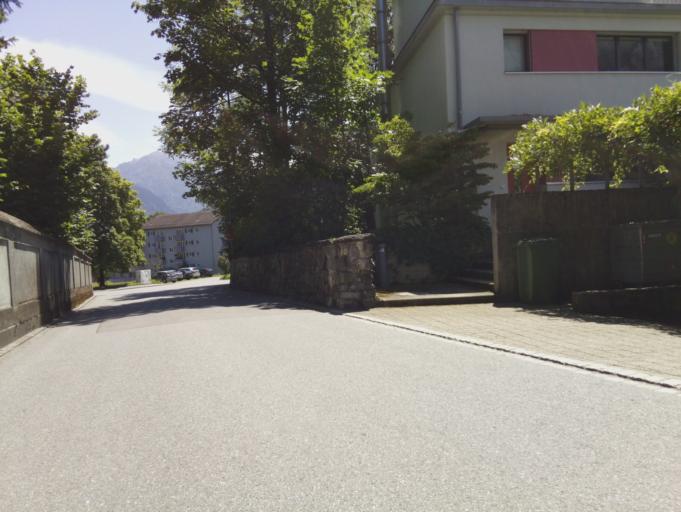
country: CH
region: Glarus
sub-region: Glarus
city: Glarus
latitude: 47.0397
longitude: 9.0623
